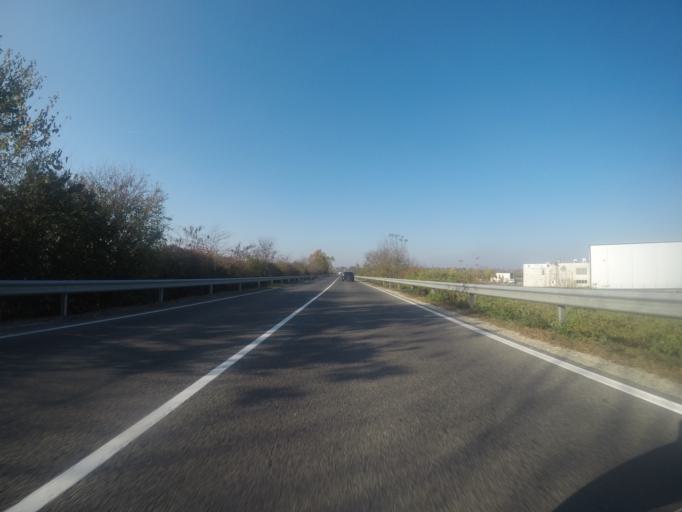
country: HU
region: Fejer
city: Ercsi
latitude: 47.2320
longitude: 18.8926
